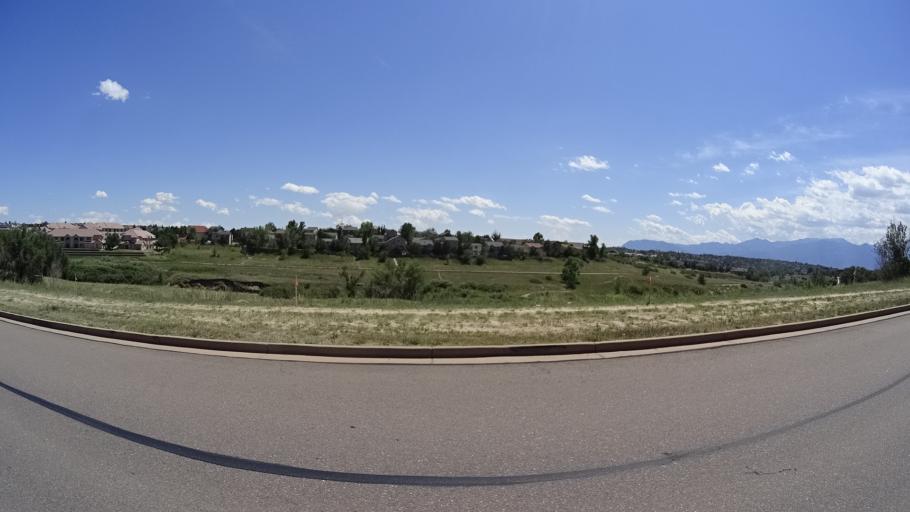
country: US
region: Colorado
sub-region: El Paso County
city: Black Forest
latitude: 38.9404
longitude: -104.7432
